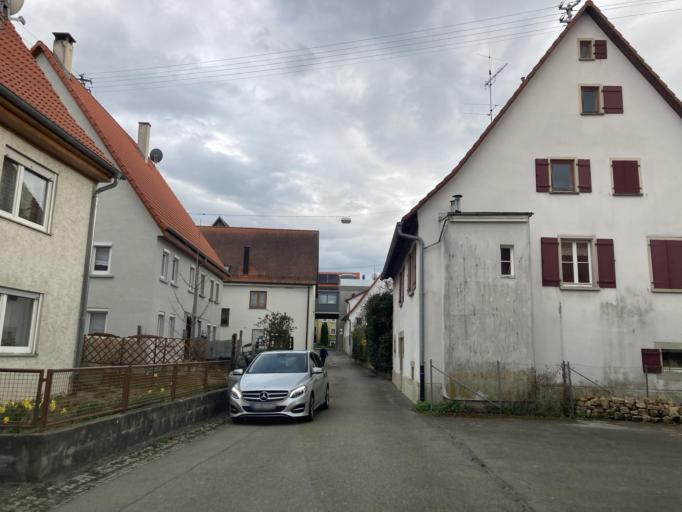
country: DE
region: Baden-Wuerttemberg
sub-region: Tuebingen Region
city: Hirrlingen
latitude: 48.4495
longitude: 8.8800
